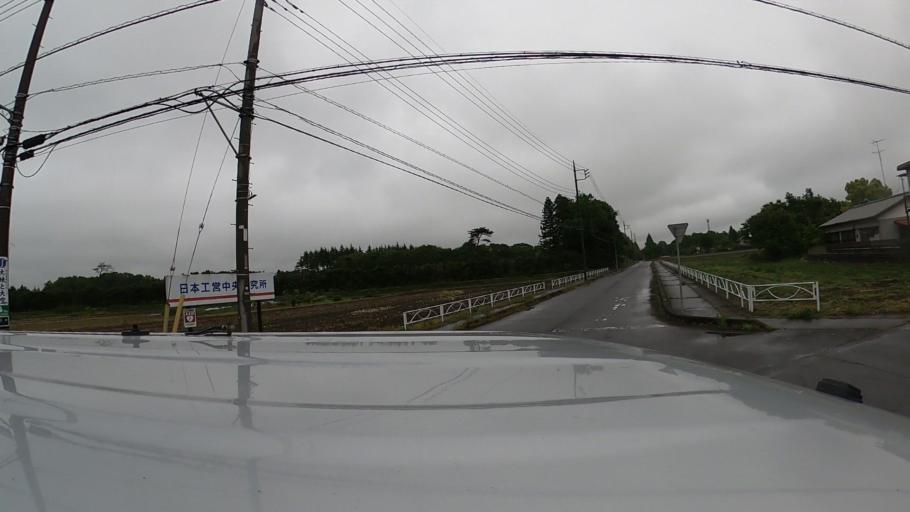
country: JP
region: Ibaraki
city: Ushiku
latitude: 36.0098
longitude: 140.1098
